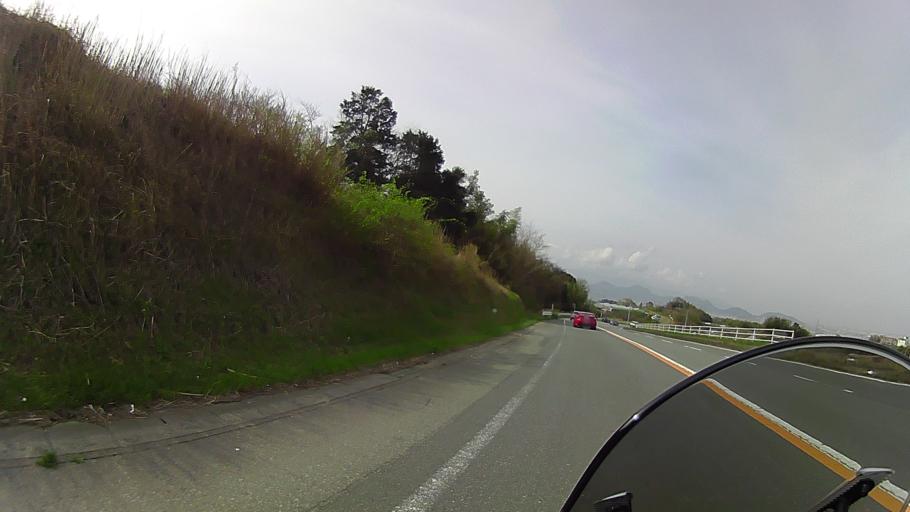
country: JP
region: Shizuoka
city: Mishima
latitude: 35.1383
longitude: 138.9700
